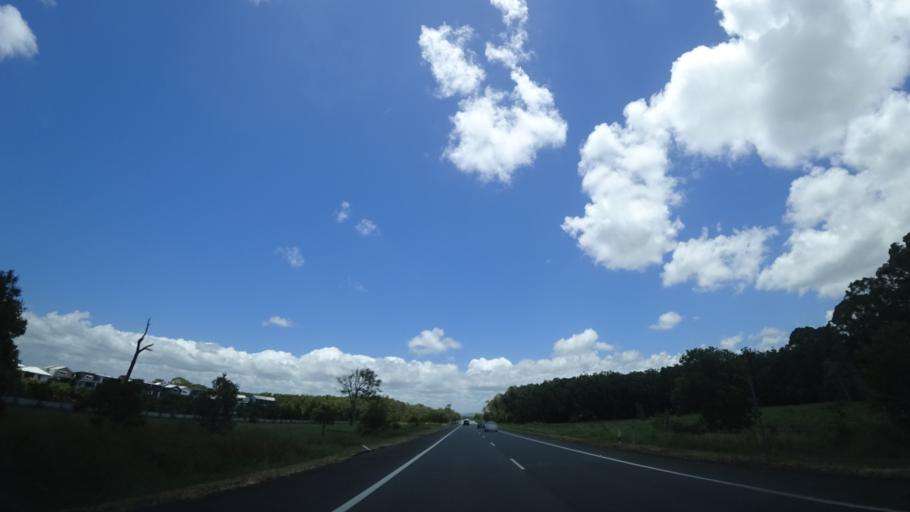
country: AU
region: Queensland
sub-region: Sunshine Coast
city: Little Mountain
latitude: -26.7658
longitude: 153.0990
